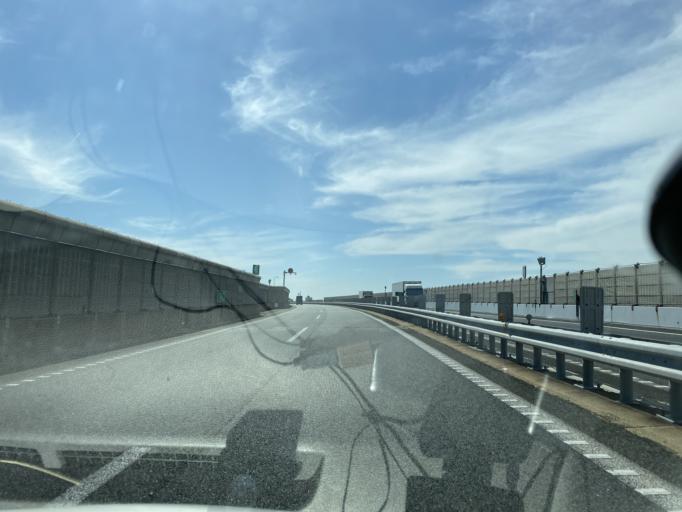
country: JP
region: Osaka
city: Ikeda
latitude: 34.8022
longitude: 135.4369
